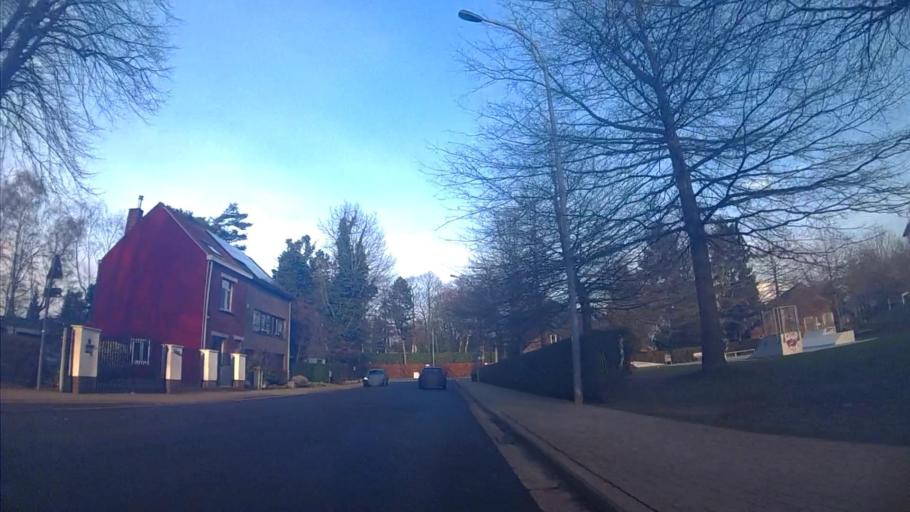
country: BE
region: Flanders
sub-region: Provincie Oost-Vlaanderen
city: Destelbergen
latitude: 51.0672
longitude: 3.7746
